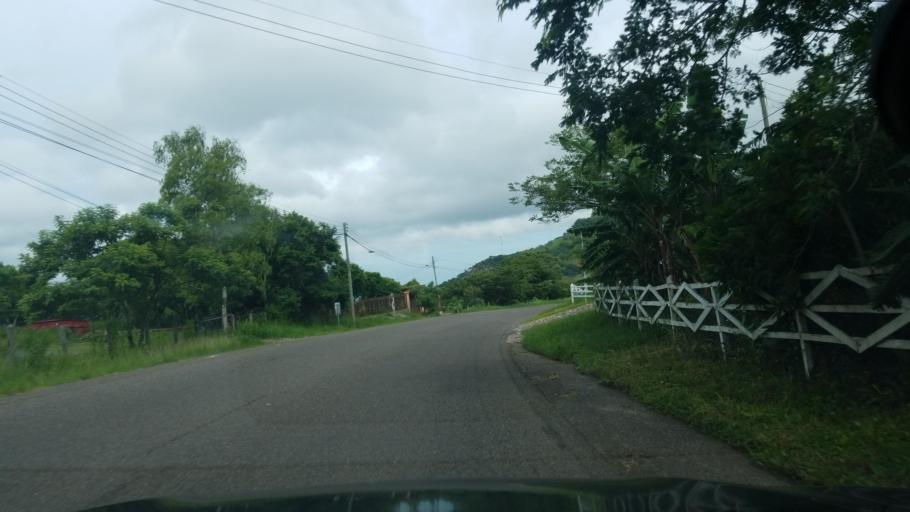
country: HN
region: Choluteca
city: Corpus
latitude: 13.3695
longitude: -86.9380
